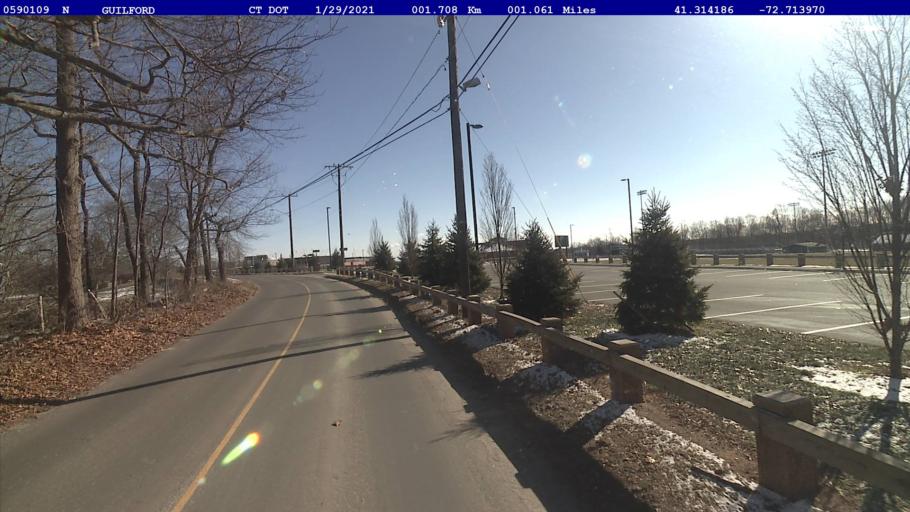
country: US
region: Connecticut
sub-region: New Haven County
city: Guilford
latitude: 41.3142
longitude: -72.7139
